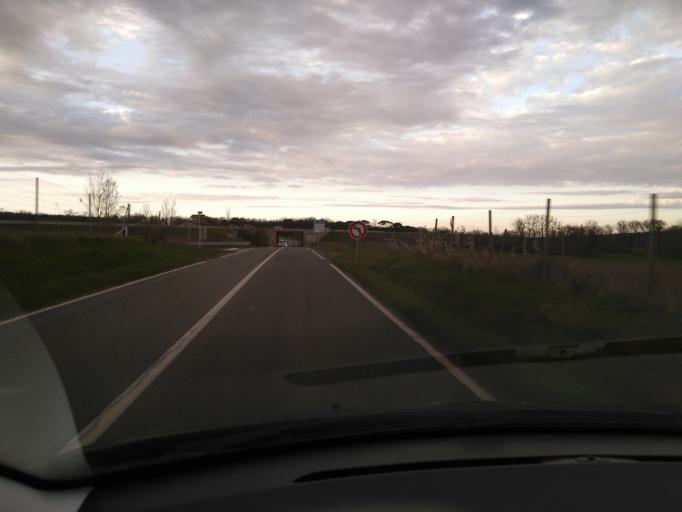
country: FR
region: Midi-Pyrenees
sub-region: Departement de la Haute-Garonne
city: La Salvetat-Saint-Gilles
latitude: 43.5848
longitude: 1.2681
